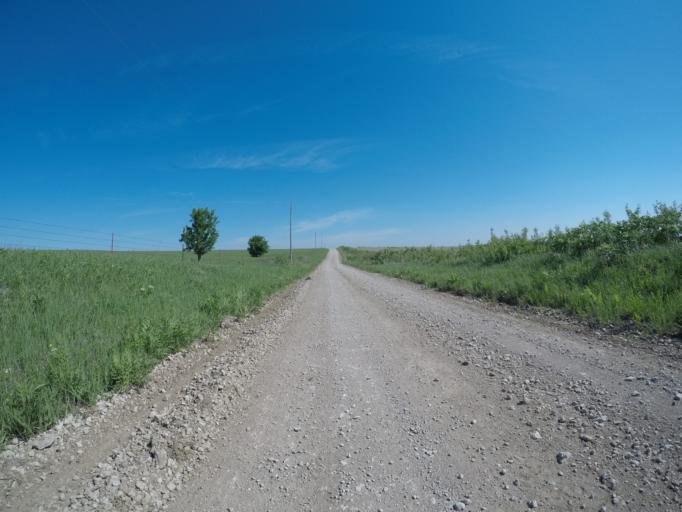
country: US
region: Kansas
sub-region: Wabaunsee County
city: Alma
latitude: 38.9537
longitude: -96.1137
